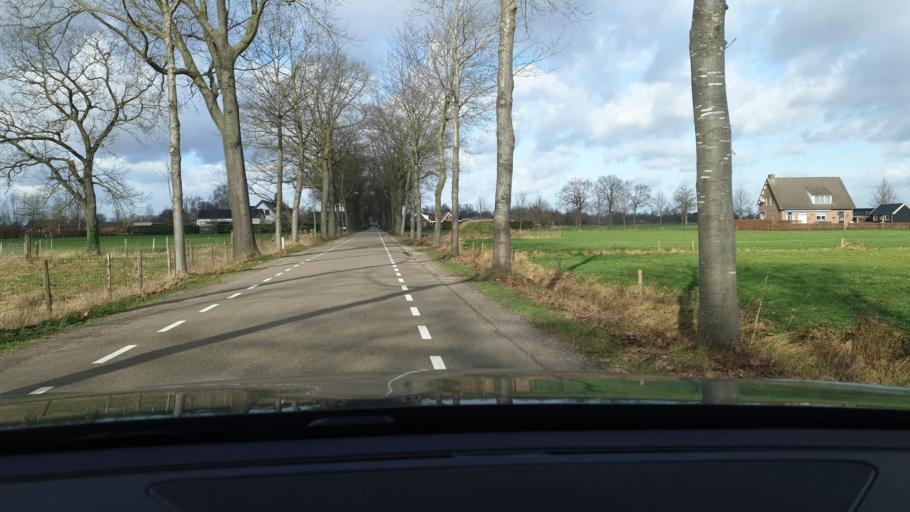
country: NL
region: North Brabant
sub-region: Gemeente Sint-Michielsgestel
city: Sint-Michielsgestel
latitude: 51.6440
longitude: 5.3820
